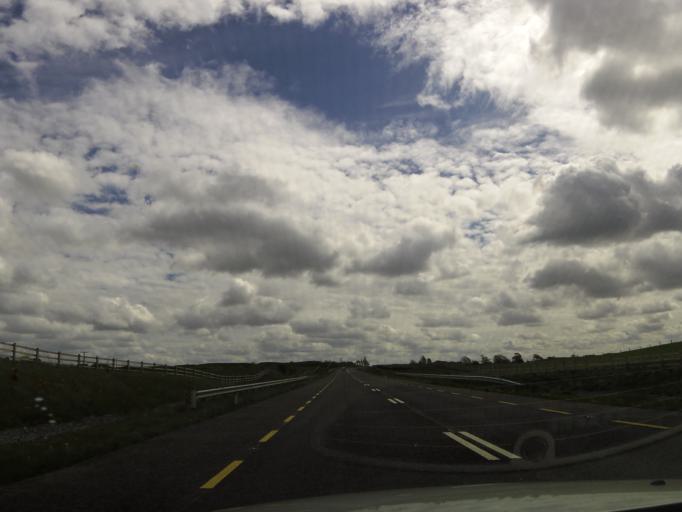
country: IE
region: Connaught
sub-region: County Galway
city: Tuam
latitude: 53.5749
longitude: -8.8448
